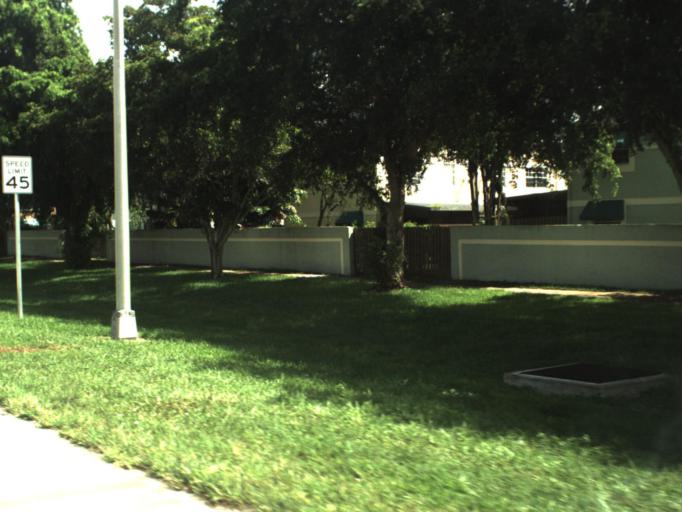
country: US
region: Florida
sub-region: Broward County
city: Sunshine Ranches
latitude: 26.0534
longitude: -80.3131
